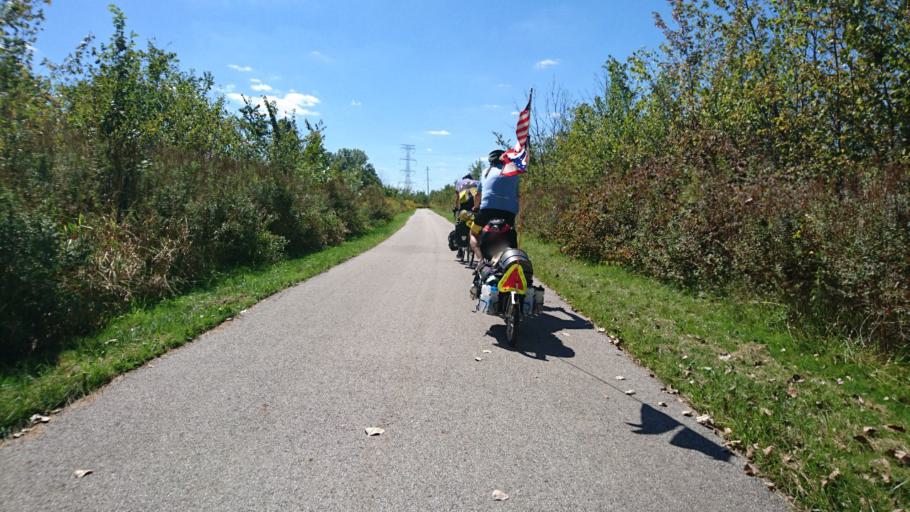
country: US
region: Illinois
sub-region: Cook County
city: Lansing
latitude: 41.5471
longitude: -87.5663
